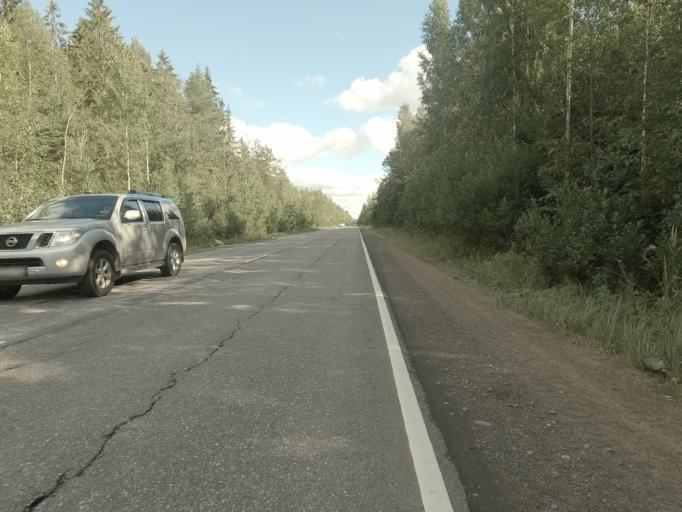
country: RU
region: Leningrad
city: Shcheglovo
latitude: 60.0018
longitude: 30.8692
